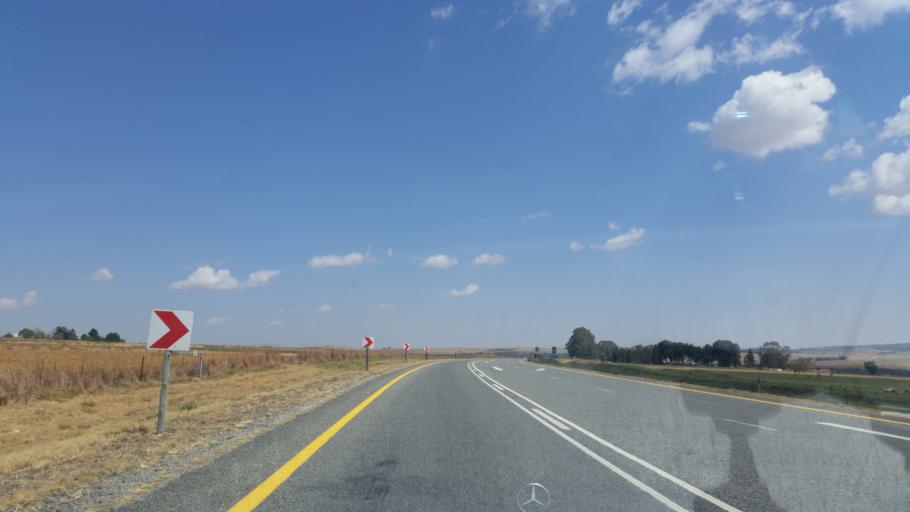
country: ZA
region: Orange Free State
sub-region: Thabo Mofutsanyana District Municipality
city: Bethlehem
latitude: -28.2750
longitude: 28.0996
